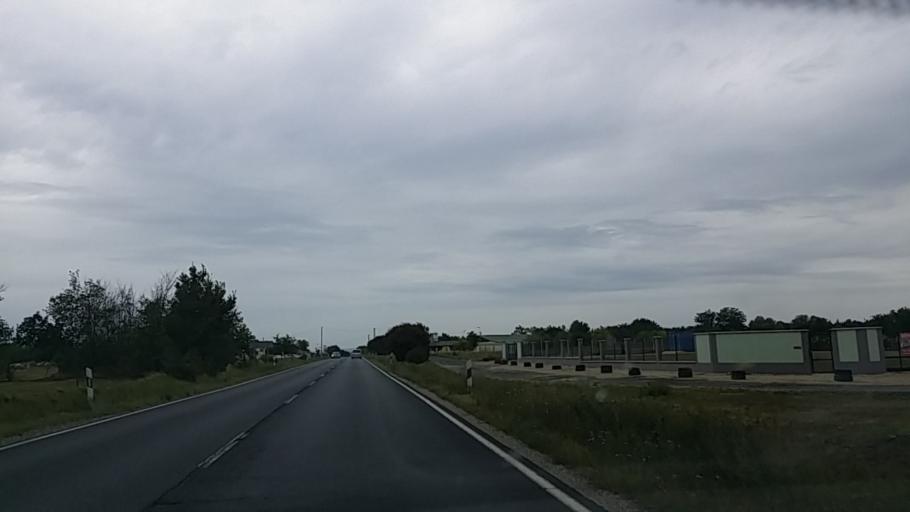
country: HU
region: Gyor-Moson-Sopron
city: Fertoszentmiklos
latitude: 47.5876
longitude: 16.8676
